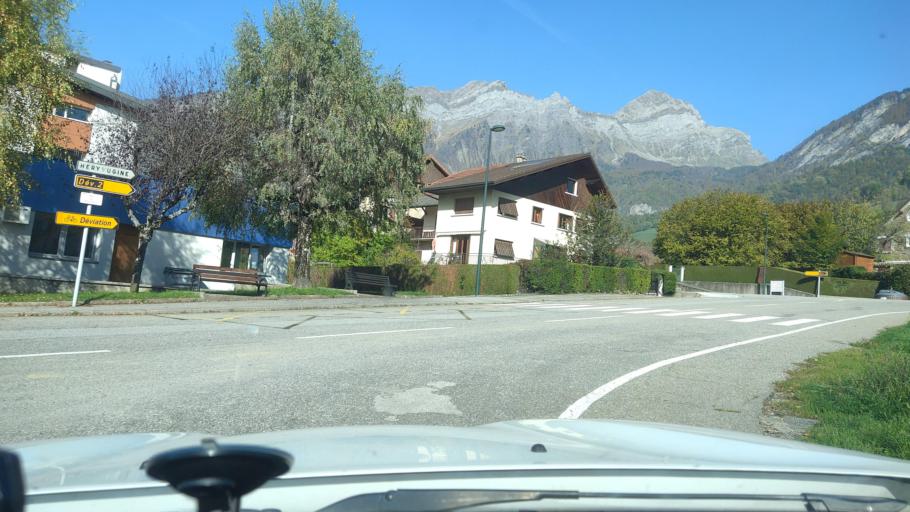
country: FR
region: Rhone-Alpes
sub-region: Departement de la Savoie
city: Ugine
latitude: 45.7517
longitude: 6.4229
